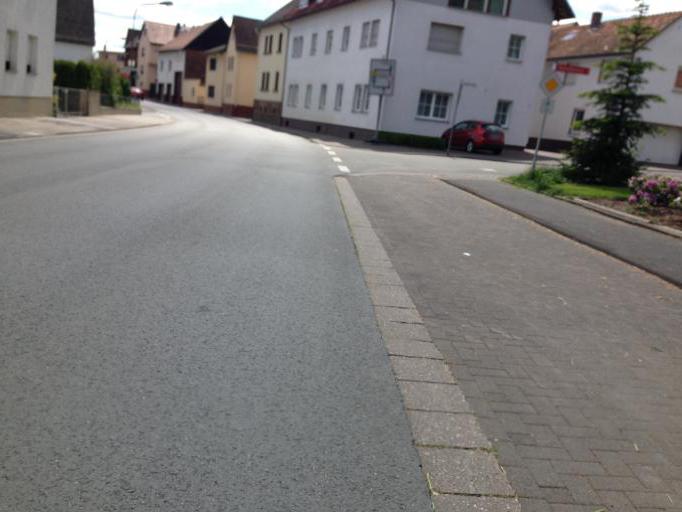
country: DE
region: Hesse
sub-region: Regierungsbezirk Giessen
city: Heuchelheim
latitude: 50.5914
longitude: 8.6117
